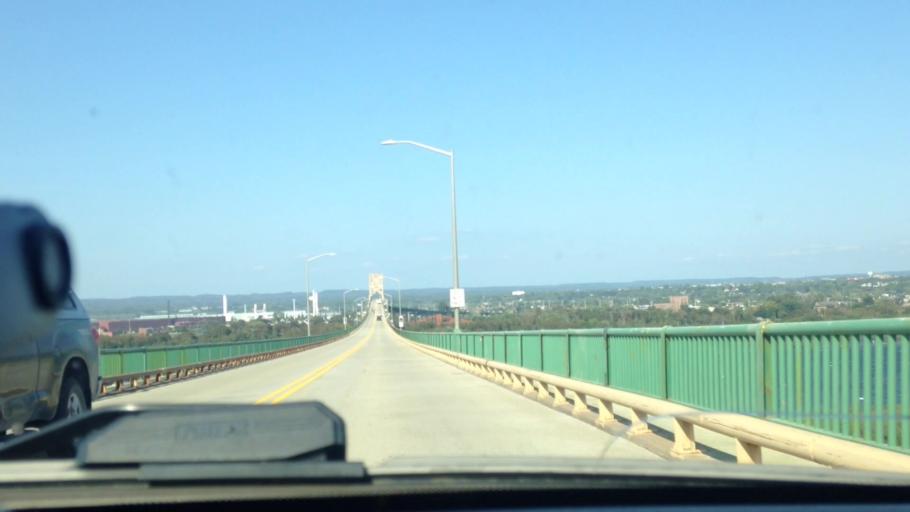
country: US
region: Michigan
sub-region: Chippewa County
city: Sault Ste. Marie
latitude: 46.5048
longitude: -84.3623
